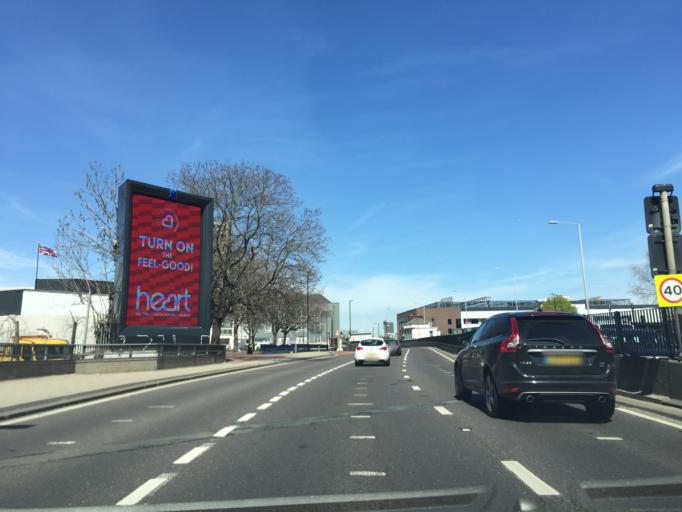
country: GB
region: England
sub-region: Greater London
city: Poplar
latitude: 51.5213
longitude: -0.0106
